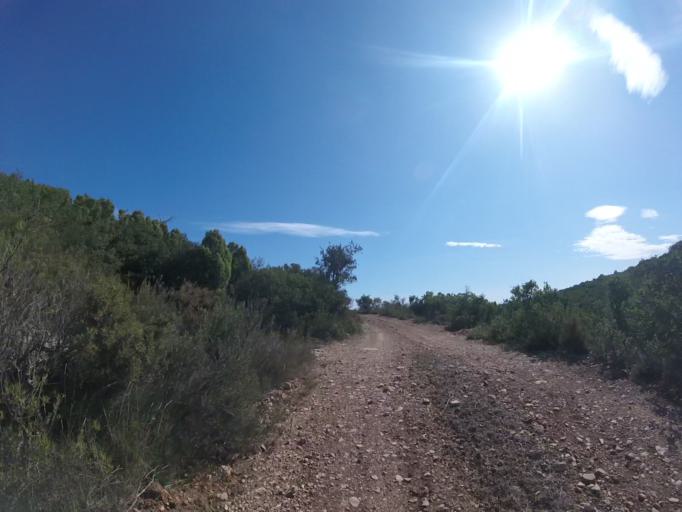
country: ES
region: Valencia
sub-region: Provincia de Castello
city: Sarratella
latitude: 40.2723
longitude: 0.0253
